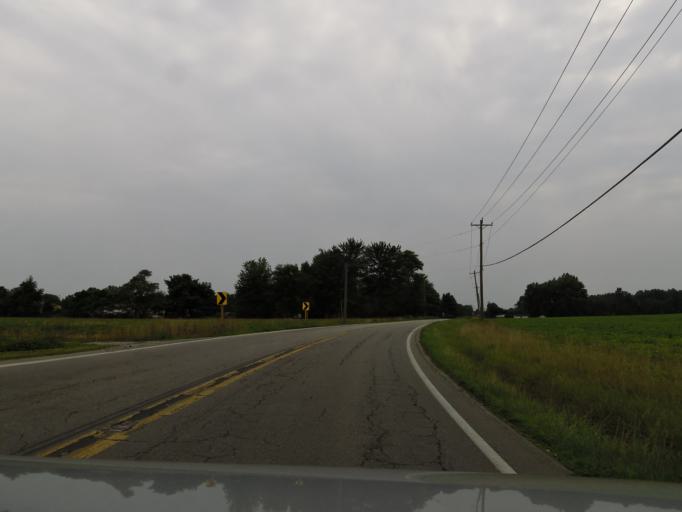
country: US
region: Ohio
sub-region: Clinton County
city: Blanchester
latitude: 39.2727
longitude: -83.9021
